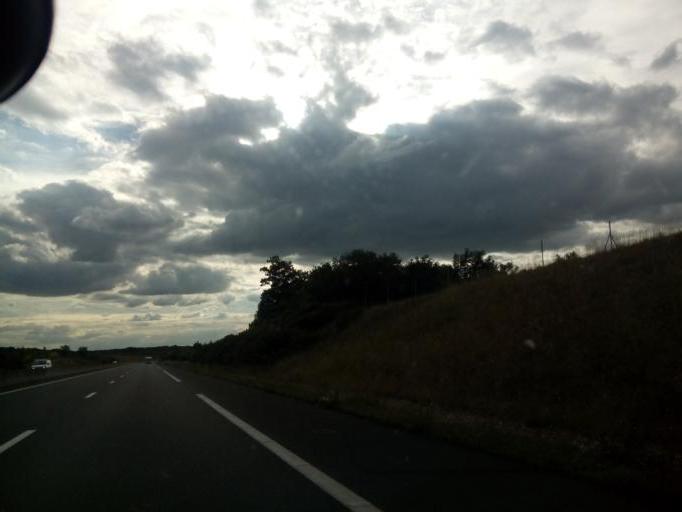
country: FR
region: Centre
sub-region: Departement d'Indre-et-Loire
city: Civray-de-Touraine
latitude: 47.2879
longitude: 1.0813
